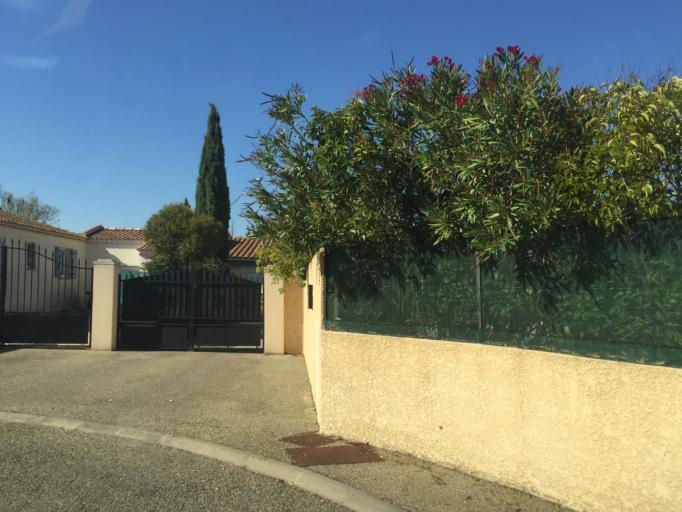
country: FR
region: Provence-Alpes-Cote d'Azur
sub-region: Departement du Vaucluse
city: Sorgues
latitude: 44.0237
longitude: 4.8675
